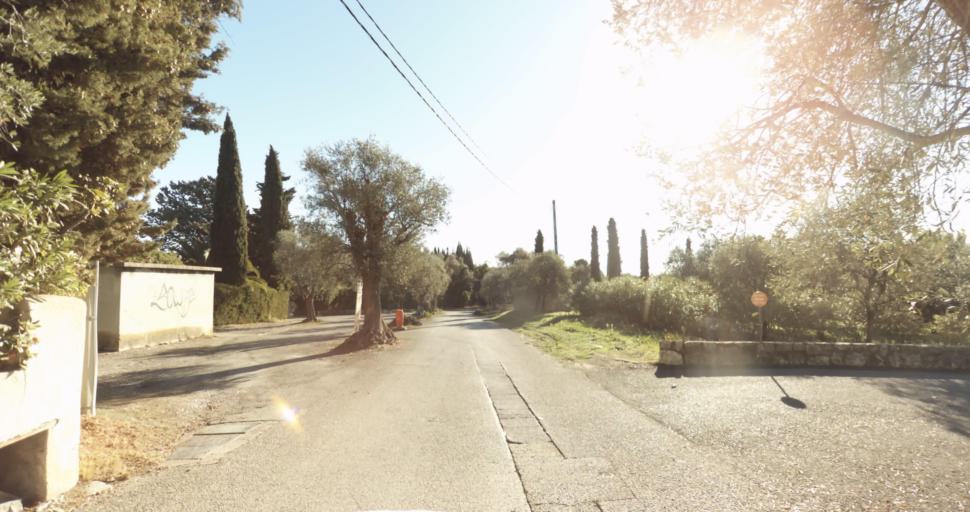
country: FR
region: Provence-Alpes-Cote d'Azur
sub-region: Departement des Alpes-Maritimes
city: Vence
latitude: 43.7216
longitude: 7.0887
